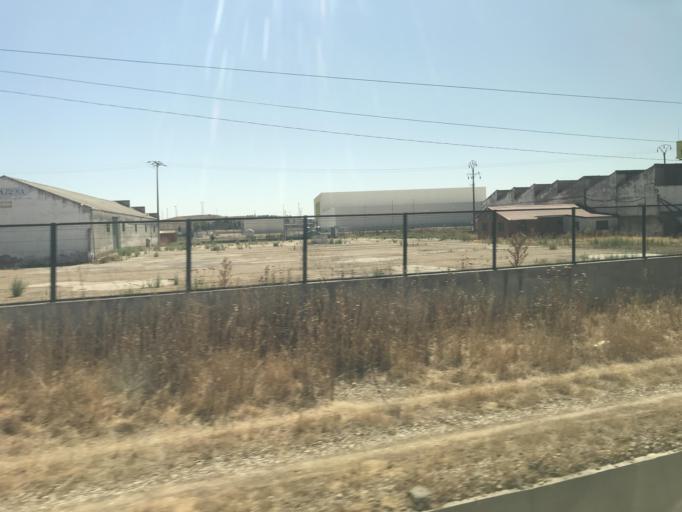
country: ES
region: Castille and Leon
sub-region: Provincia de Valladolid
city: Santovenia de Pisuerga
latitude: 41.6860
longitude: -4.6864
